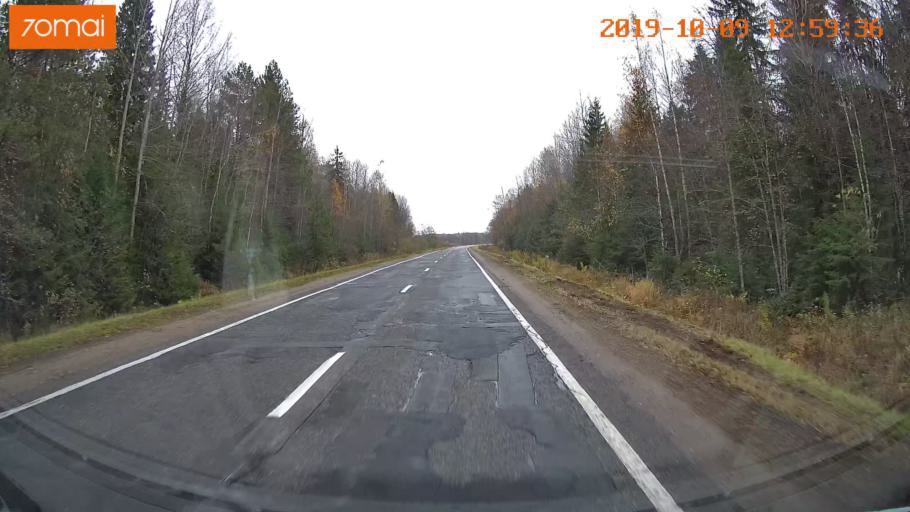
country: RU
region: Jaroslavl
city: Prechistoye
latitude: 58.3828
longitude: 40.4673
